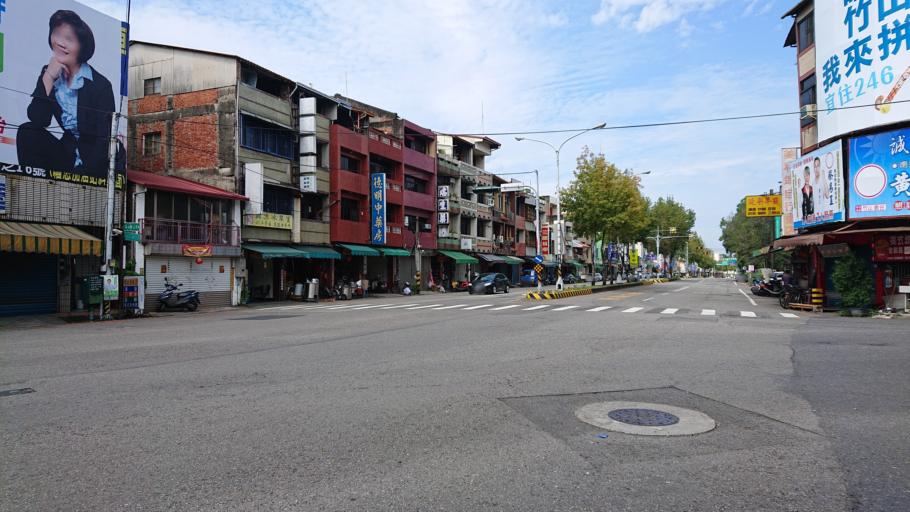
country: TW
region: Taiwan
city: Lugu
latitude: 23.7671
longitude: 120.7067
